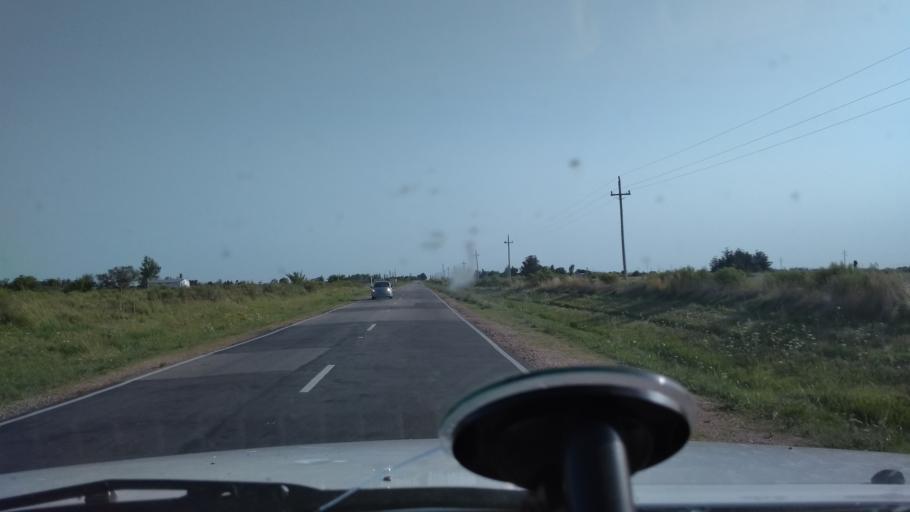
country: UY
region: Canelones
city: Santa Rosa
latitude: -34.5134
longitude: -56.0541
